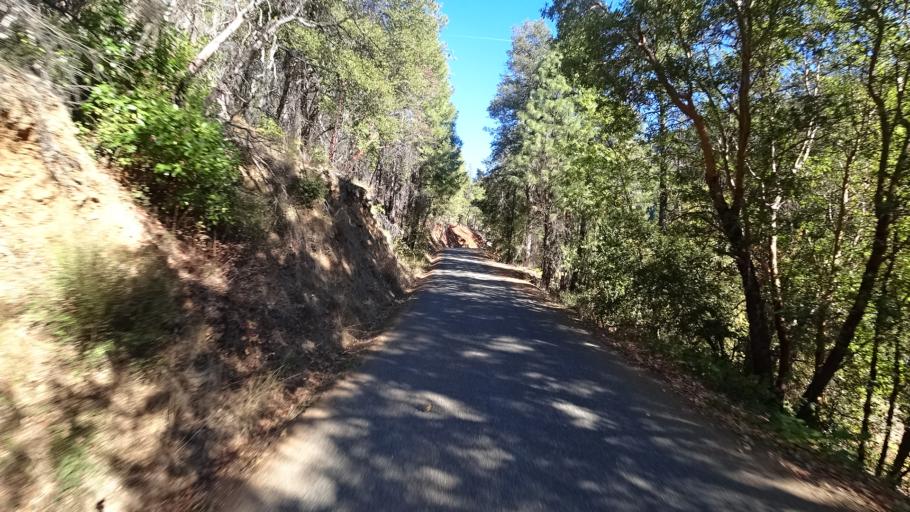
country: US
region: California
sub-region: Siskiyou County
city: Happy Camp
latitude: 41.2999
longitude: -123.2259
